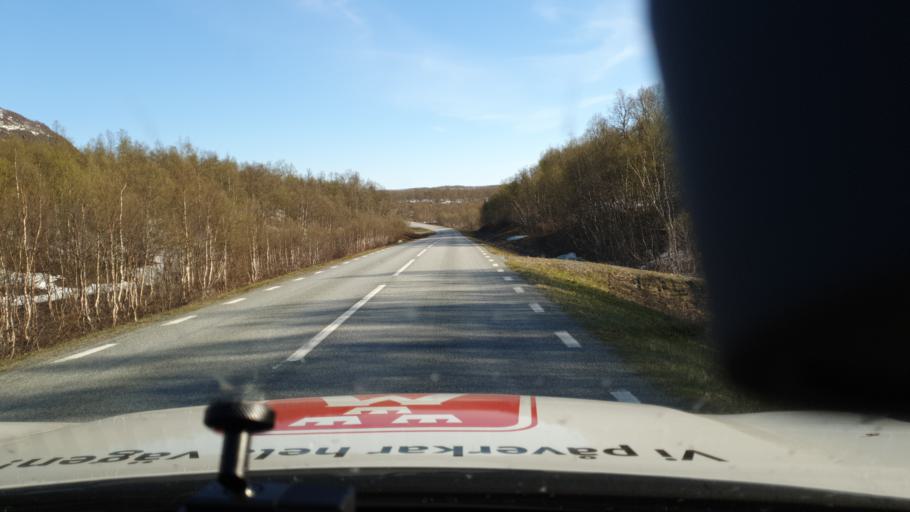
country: NO
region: Nordland
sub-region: Rana
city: Mo i Rana
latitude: 65.8940
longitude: 14.9840
